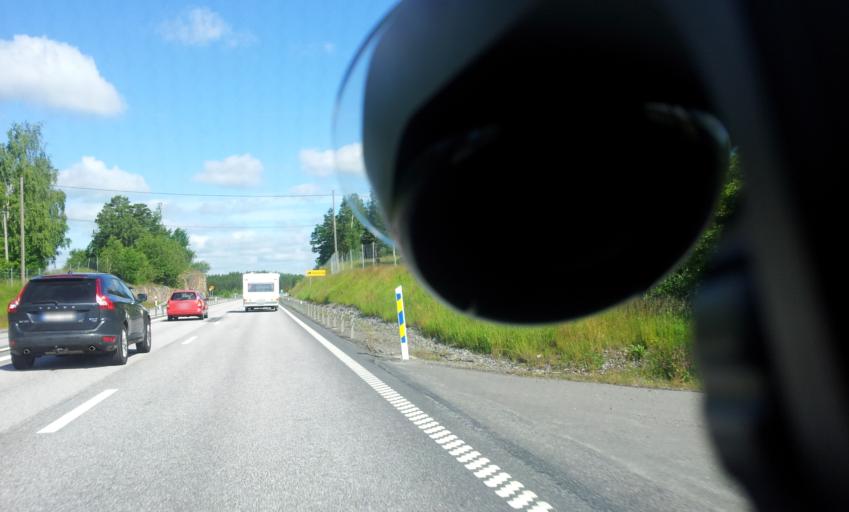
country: SE
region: OEstergoetland
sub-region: Valdemarsviks Kommun
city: Gusum
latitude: 58.3583
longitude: 16.4415
